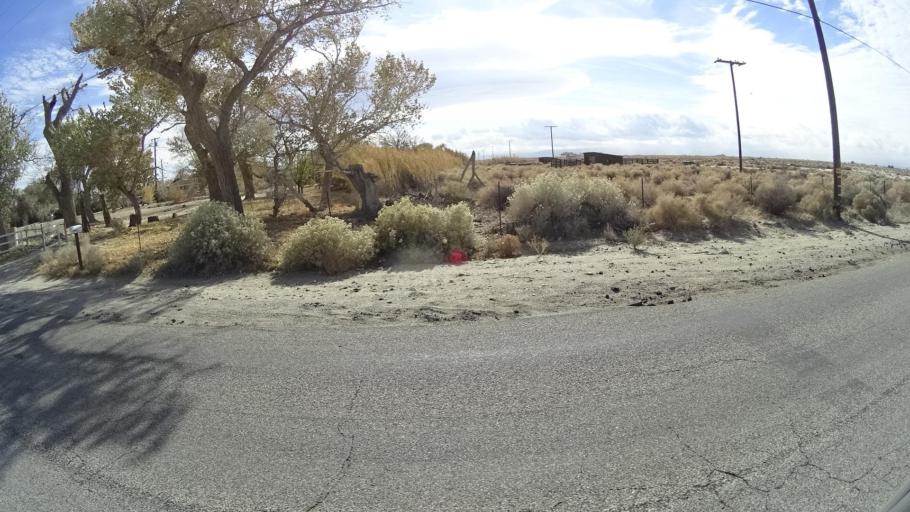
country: US
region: California
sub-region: Kern County
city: Rosamond
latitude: 34.8203
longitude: -118.1920
